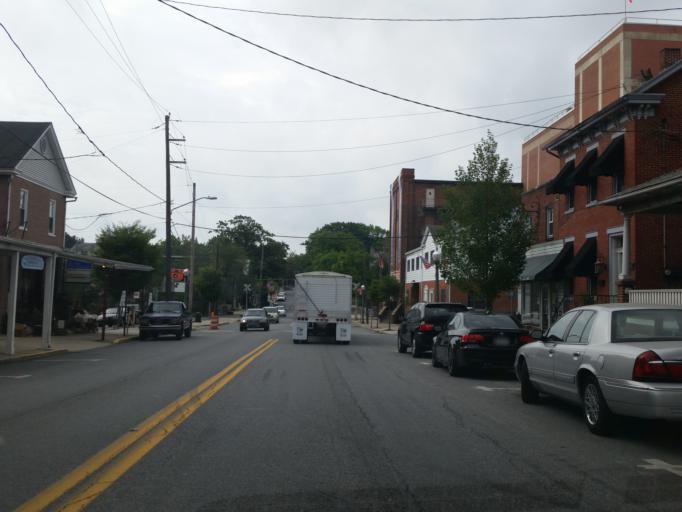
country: US
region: Pennsylvania
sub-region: Lancaster County
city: Lititz
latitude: 40.1593
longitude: -76.3076
